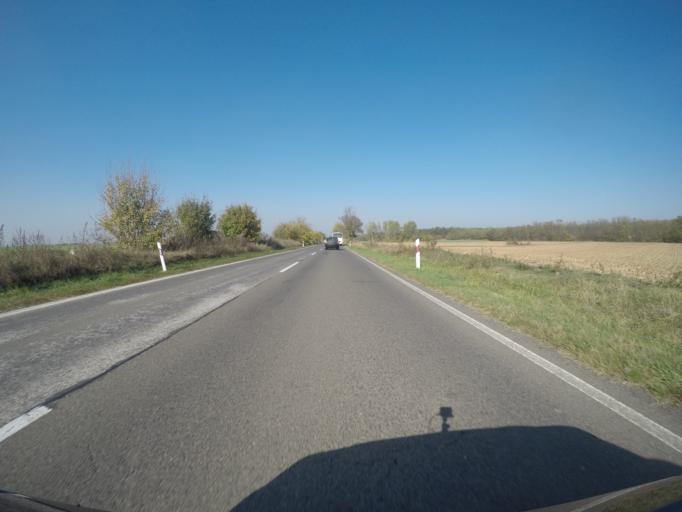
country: HU
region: Tolna
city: Szedres
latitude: 46.5029
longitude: 18.6693
